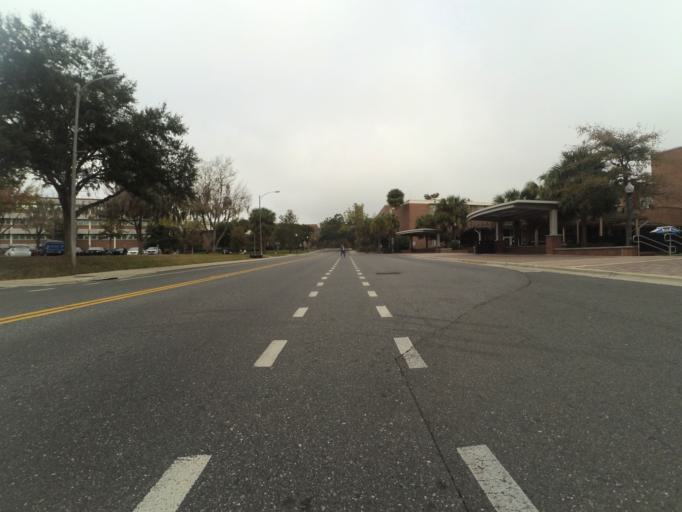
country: US
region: Florida
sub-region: Alachua County
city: Gainesville
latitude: 29.6459
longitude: -82.3434
